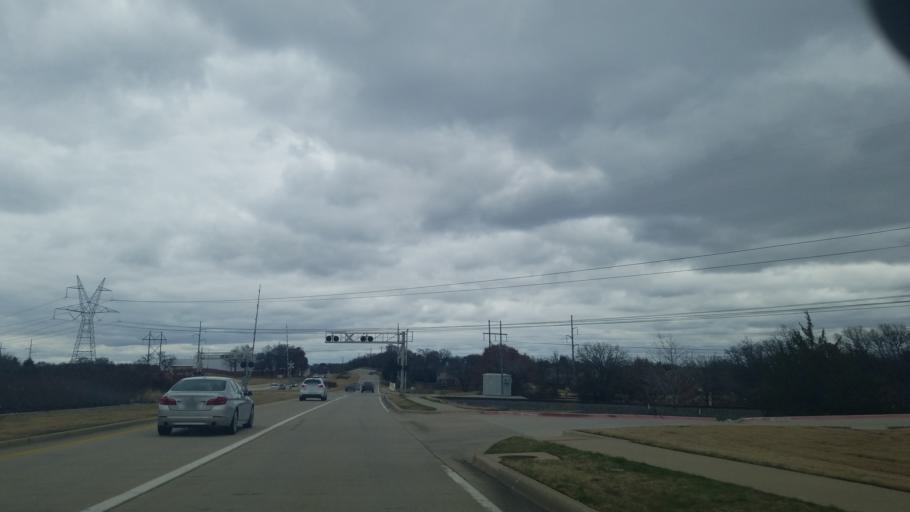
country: US
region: Texas
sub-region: Denton County
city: Copper Canyon
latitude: 33.0861
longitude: -97.0782
